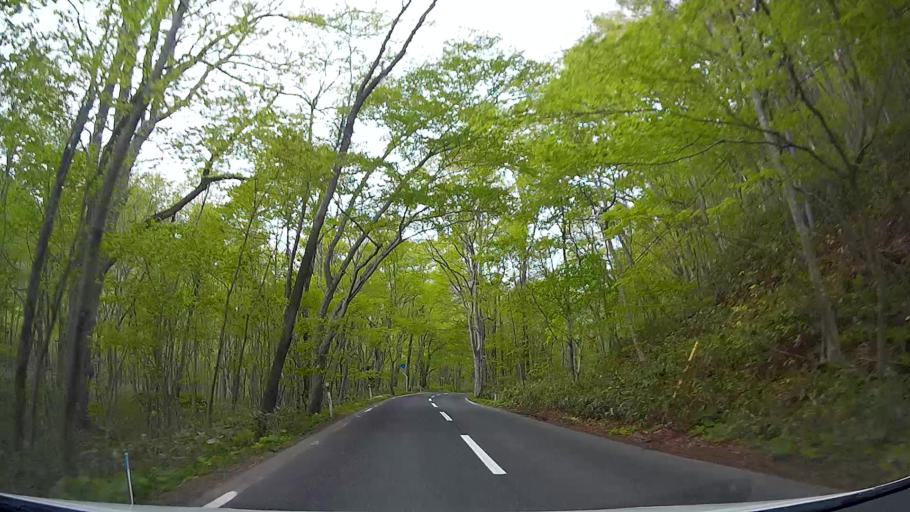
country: JP
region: Aomori
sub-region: Aomori Shi
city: Furudate
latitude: 40.5720
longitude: 140.9785
